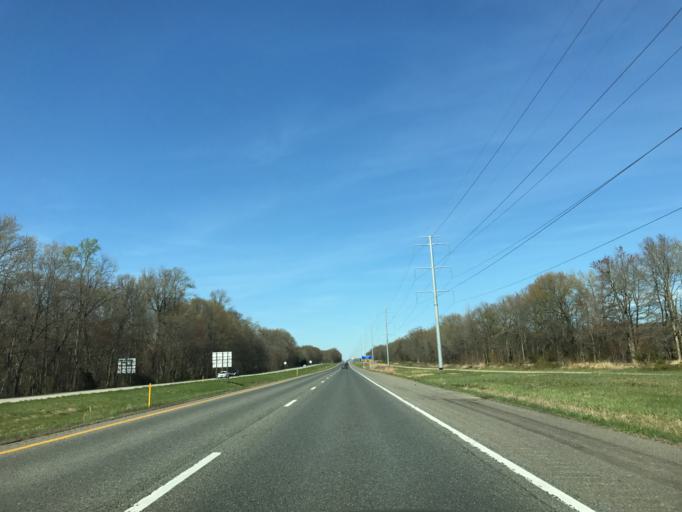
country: US
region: Maryland
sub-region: Queen Anne's County
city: Centreville
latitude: 39.0650
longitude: -75.9907
